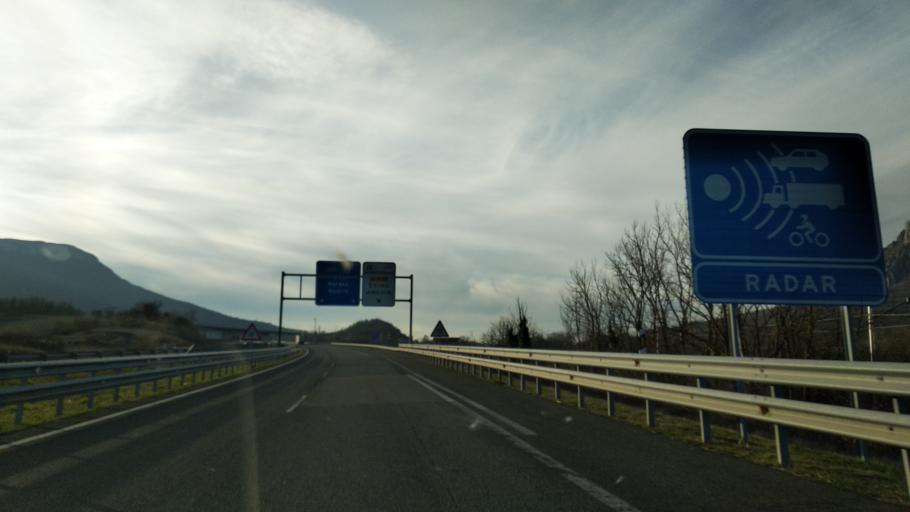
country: ES
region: Navarre
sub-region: Provincia de Navarra
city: Ziordia
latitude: 42.8662
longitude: -2.2442
